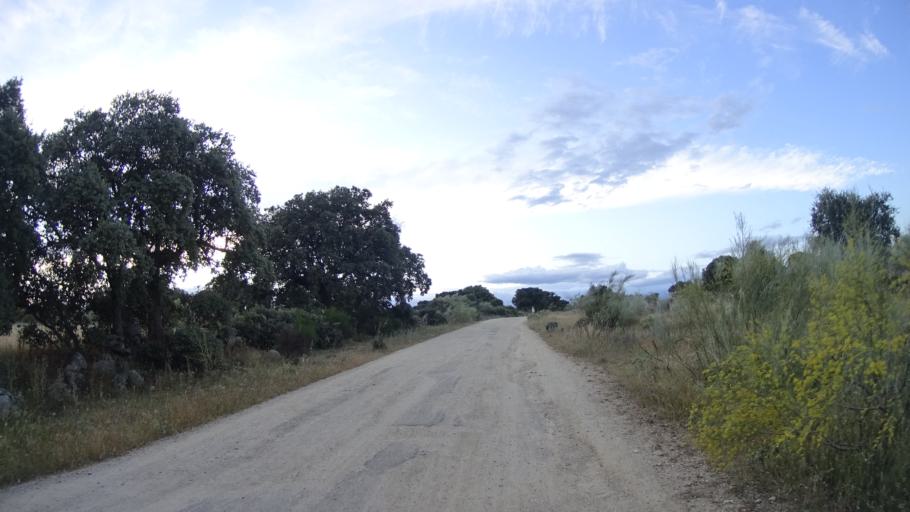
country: ES
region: Madrid
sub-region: Provincia de Madrid
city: Colmenarejo
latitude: 40.5396
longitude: -4.0104
